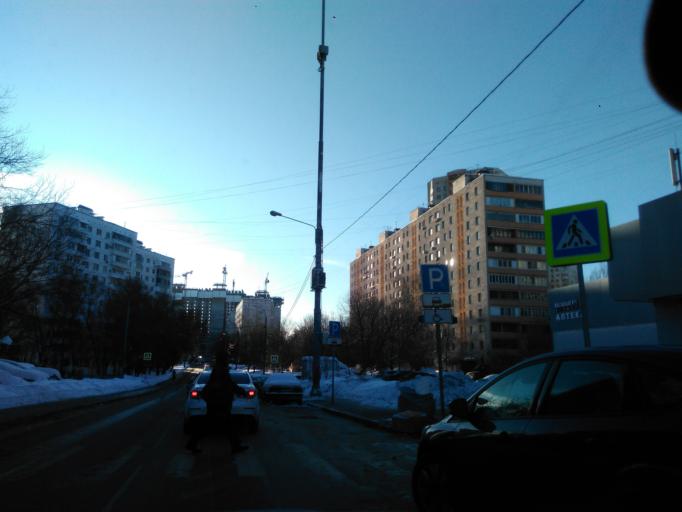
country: RU
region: Moscow
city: Zapadnoye Degunino
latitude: 55.8656
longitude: 37.5359
